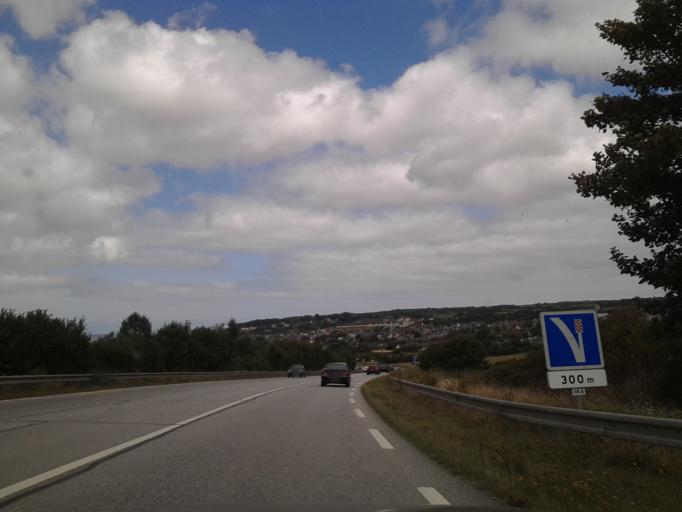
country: FR
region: Lower Normandy
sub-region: Departement de la Manche
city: Tourlaville
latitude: 49.6290
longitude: -1.5813
